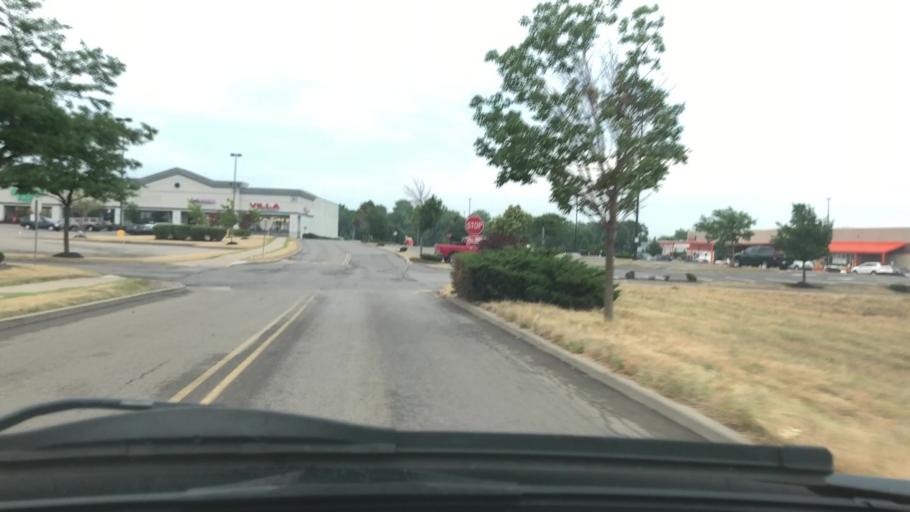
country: US
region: New York
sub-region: Erie County
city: Sloan
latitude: 42.9037
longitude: -78.7807
